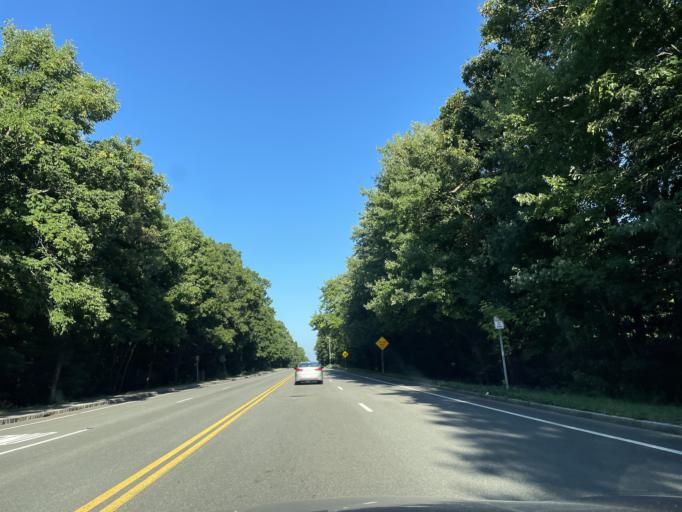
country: US
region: Massachusetts
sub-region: Bristol County
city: Easton
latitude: 42.0276
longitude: -71.1729
